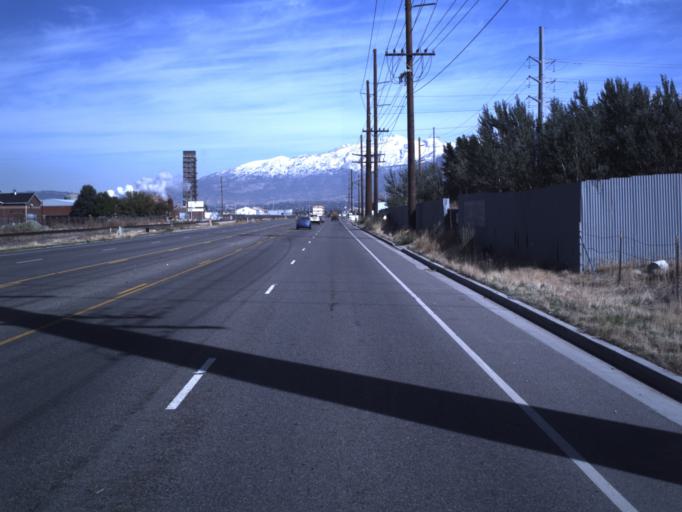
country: US
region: Utah
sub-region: Utah County
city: Lindon
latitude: 40.3157
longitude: -111.7353
